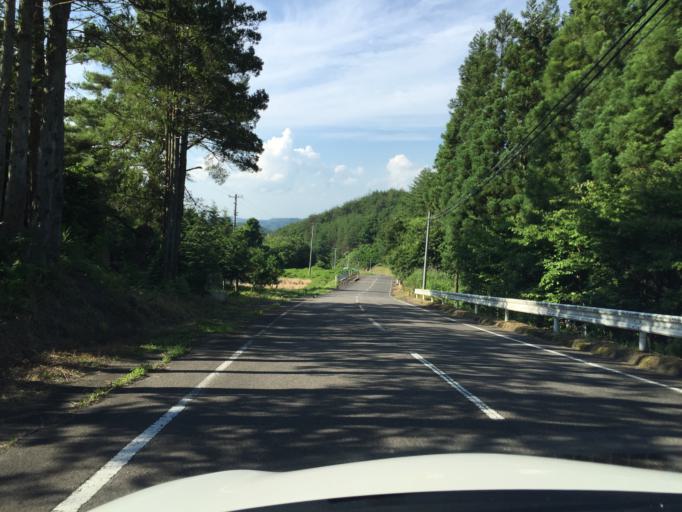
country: JP
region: Fukushima
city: Sukagawa
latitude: 37.2767
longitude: 140.5038
